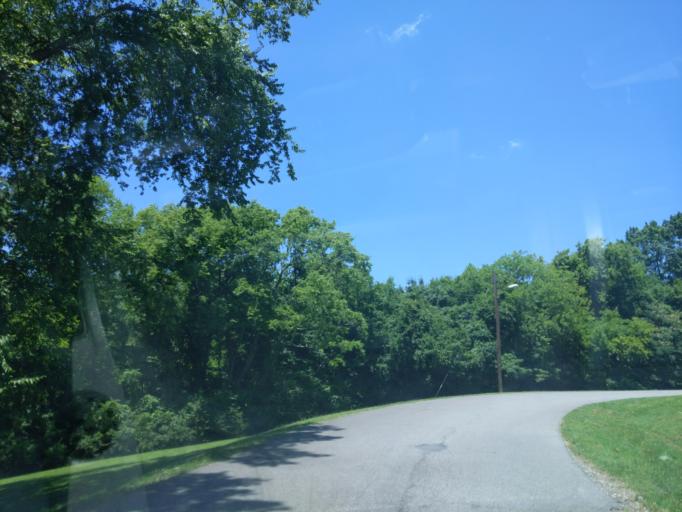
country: US
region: Tennessee
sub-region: Davidson County
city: Nashville
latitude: 36.1642
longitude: -86.7444
